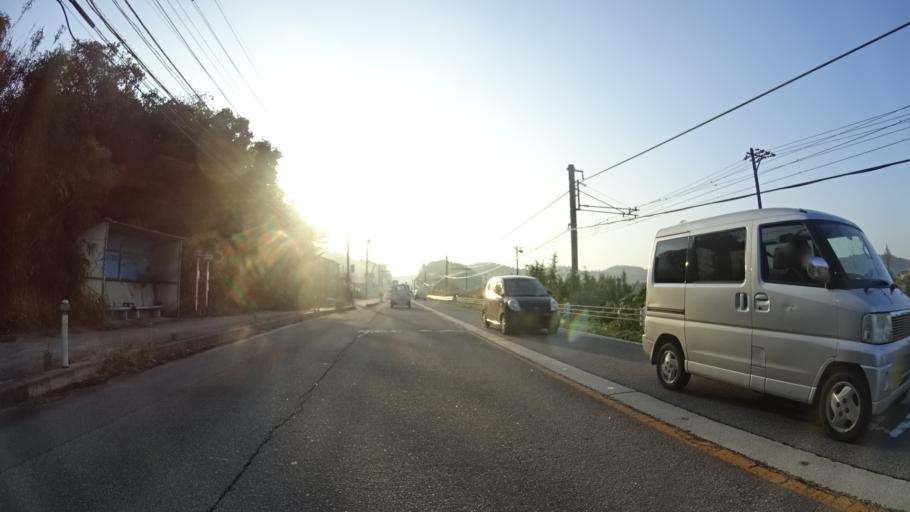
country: JP
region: Ishikawa
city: Nanao
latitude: 37.0621
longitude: 136.9422
